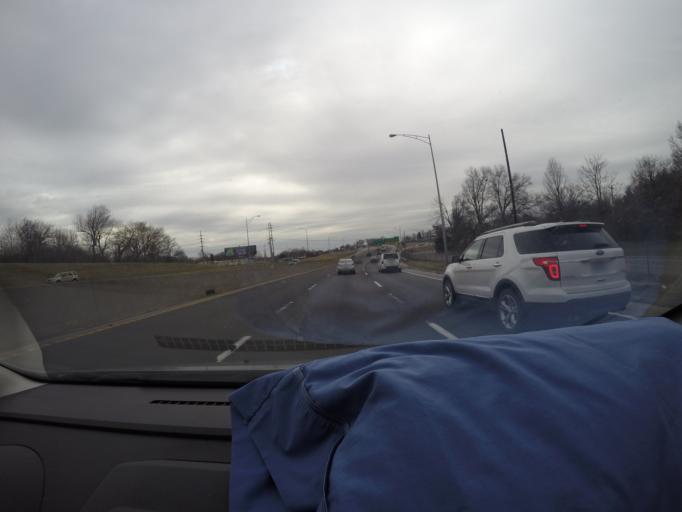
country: US
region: Missouri
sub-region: Saint Louis County
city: Pine Lawn
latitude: 38.7054
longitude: -90.2717
